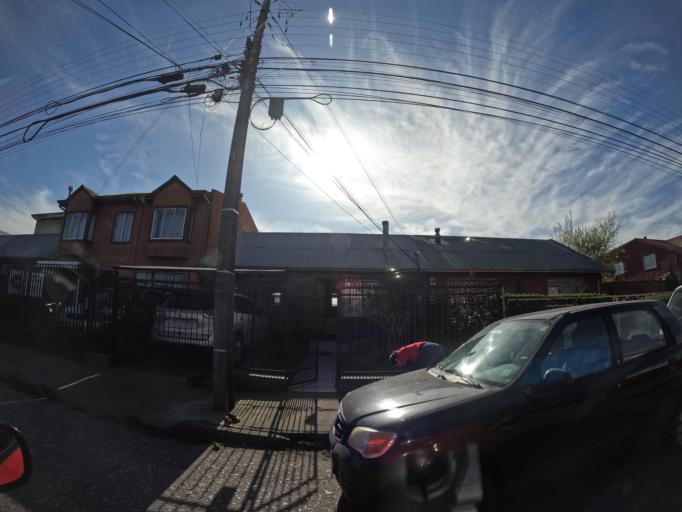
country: CL
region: Biobio
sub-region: Provincia de Concepcion
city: Concepcion
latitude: -36.8066
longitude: -73.0762
